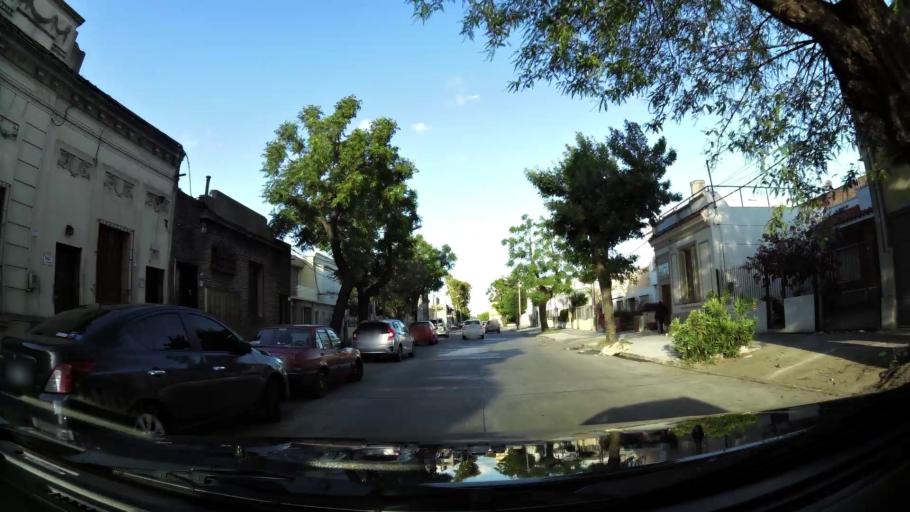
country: UY
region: Montevideo
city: Montevideo
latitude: -34.8776
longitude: -56.1490
